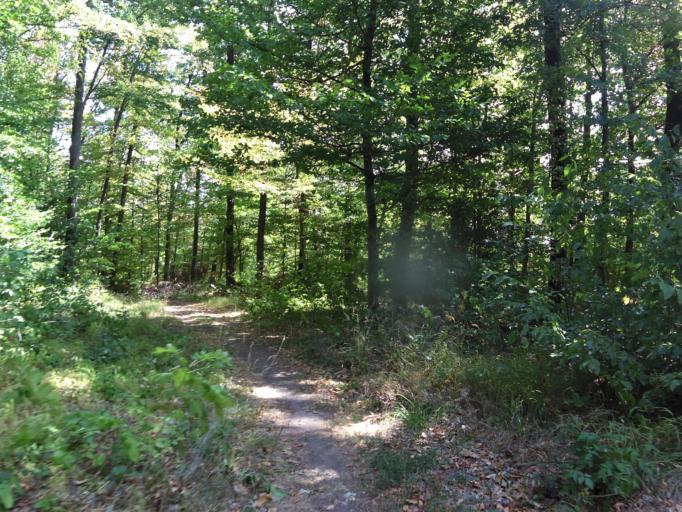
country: DE
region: Bavaria
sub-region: Regierungsbezirk Unterfranken
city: Hochberg
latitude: 49.7858
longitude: 9.8736
